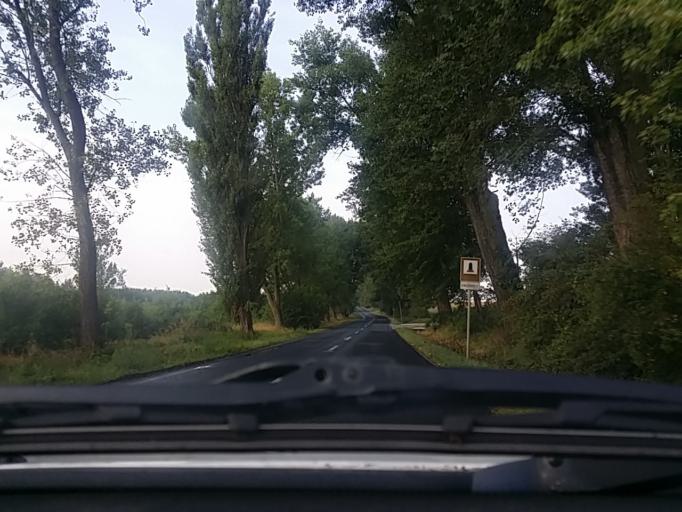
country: HU
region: Fejer
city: Szarliget
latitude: 47.4597
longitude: 18.5573
